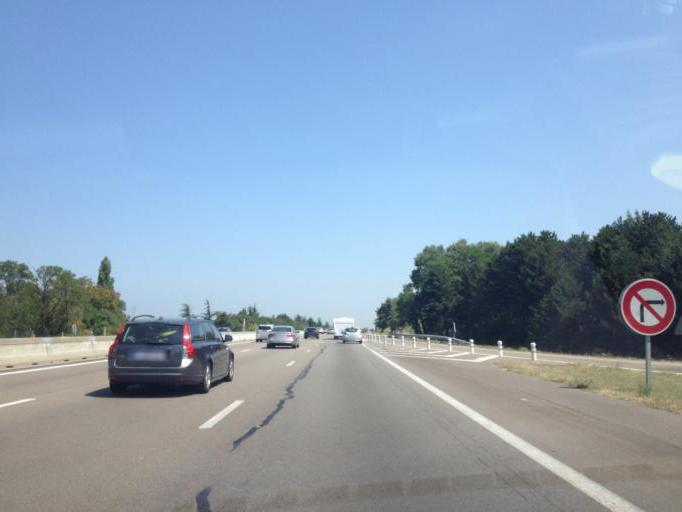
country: FR
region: Rhone-Alpes
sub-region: Departement de l'Ardeche
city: Cruas
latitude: 44.6437
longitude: 4.7921
